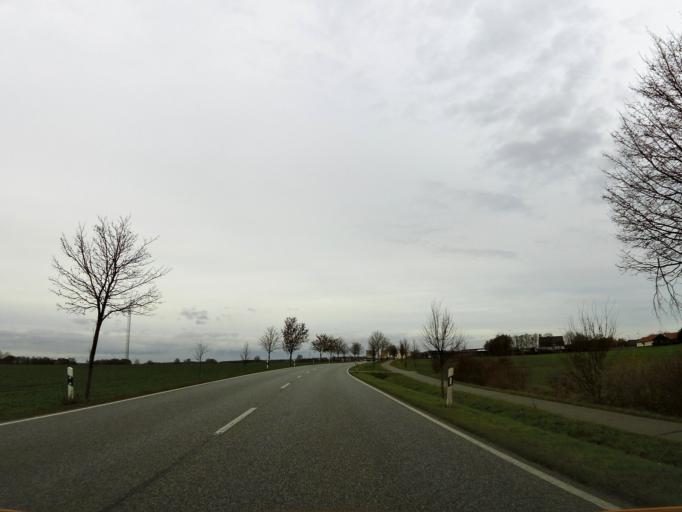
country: DE
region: Saxony-Anhalt
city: Pretzier
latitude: 52.8090
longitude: 11.2216
